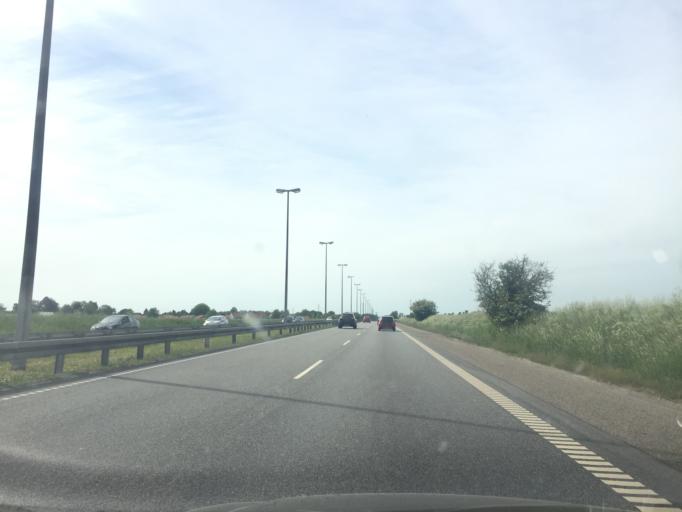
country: DK
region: Capital Region
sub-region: Hoje-Taastrup Kommune
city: Taastrup
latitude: 55.6246
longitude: 12.3162
